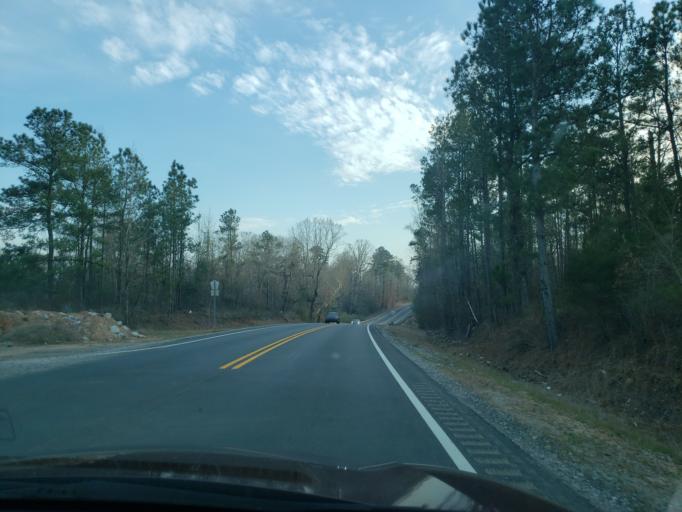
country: US
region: Alabama
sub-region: Hale County
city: Moundville
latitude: 32.8832
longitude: -87.6083
